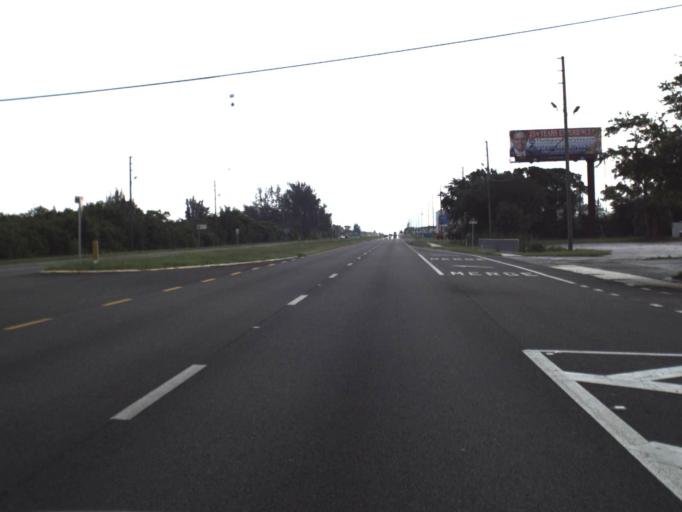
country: US
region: Florida
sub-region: Pinellas County
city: Gandy
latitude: 27.8683
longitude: -82.6221
